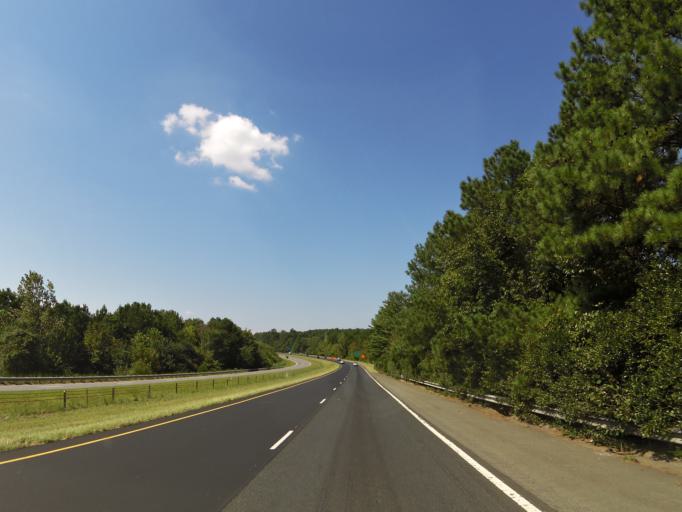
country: US
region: North Carolina
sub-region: Lincoln County
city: Lincolnton
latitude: 35.4641
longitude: -81.2199
